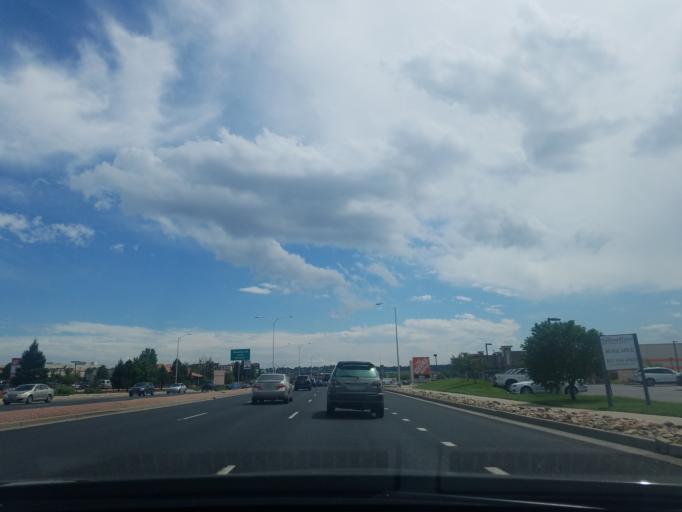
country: US
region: Colorado
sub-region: El Paso County
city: Air Force Academy
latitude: 38.9367
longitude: -104.7980
